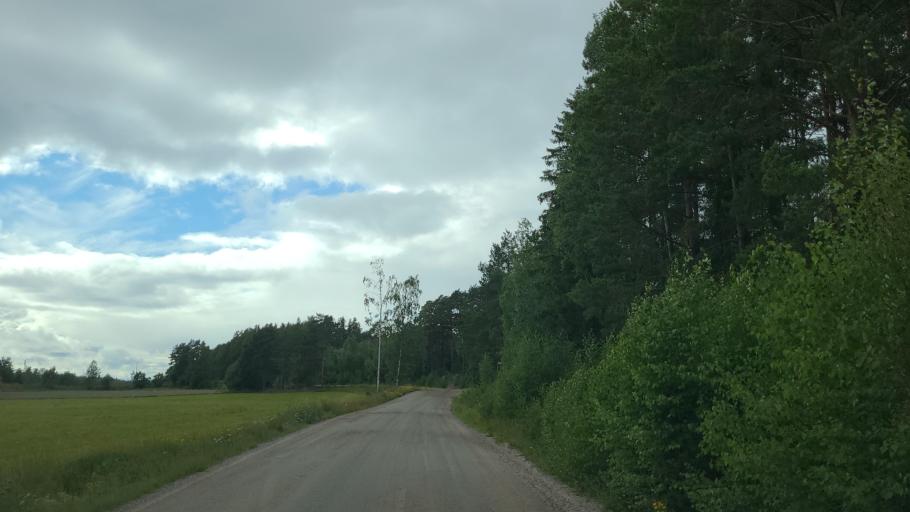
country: FI
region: Varsinais-Suomi
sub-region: Aboland-Turunmaa
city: Nagu
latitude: 60.2055
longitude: 21.8222
